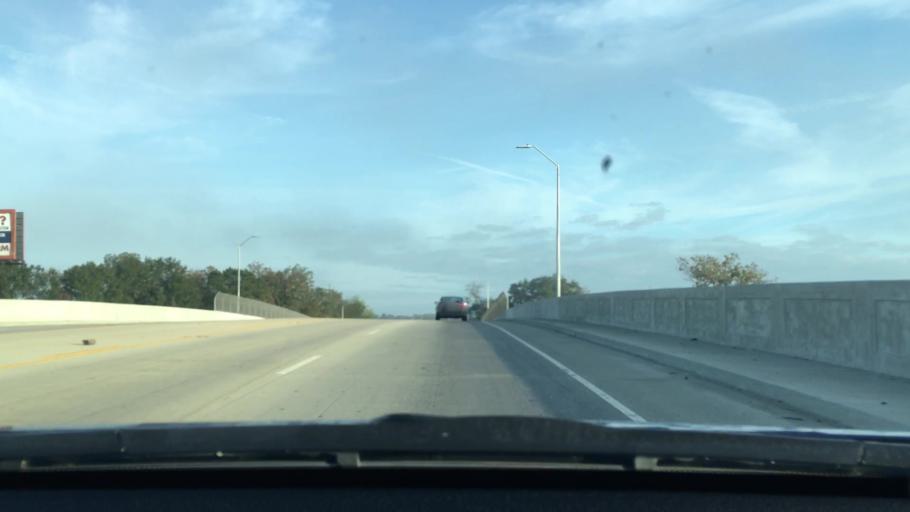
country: US
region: South Carolina
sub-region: Sumter County
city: Sumter
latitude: 33.9164
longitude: -80.3362
